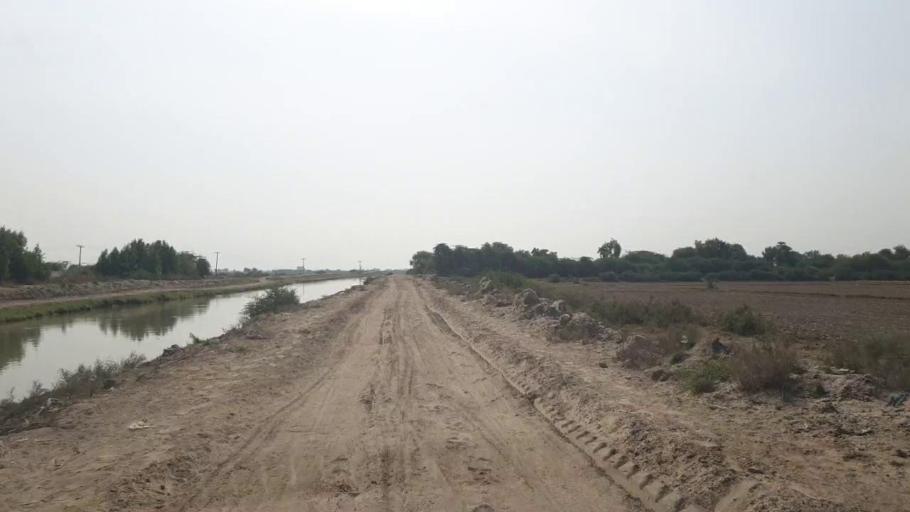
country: PK
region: Sindh
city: Badin
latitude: 24.5530
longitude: 68.8498
